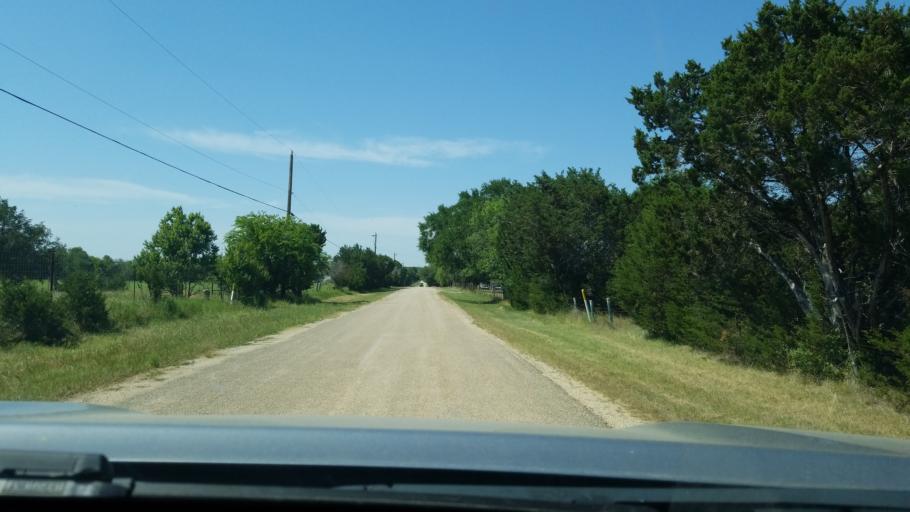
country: US
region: Texas
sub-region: Bexar County
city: Timberwood Park
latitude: 29.7459
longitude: -98.5179
